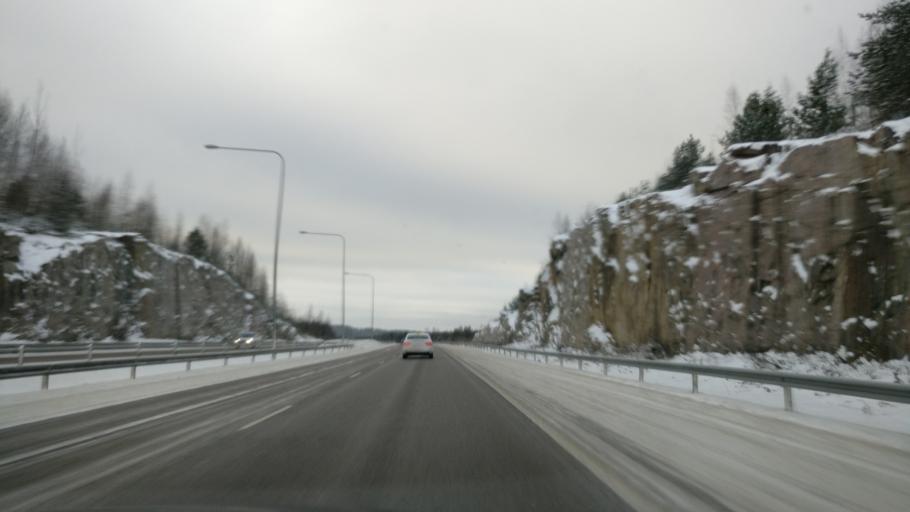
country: FI
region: Paijanne Tavastia
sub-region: Lahti
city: Lahti
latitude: 60.9642
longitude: 25.7071
